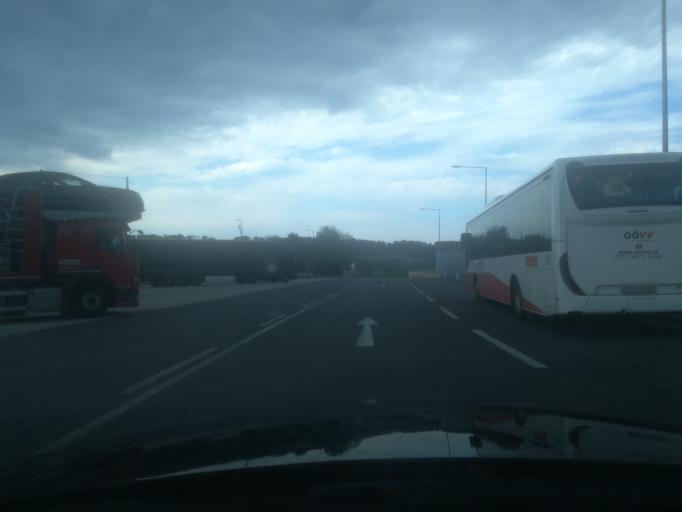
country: AT
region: Upper Austria
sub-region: Politischer Bezirk Urfahr-Umgebung
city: Engerwitzdorf
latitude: 48.3480
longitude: 14.4534
